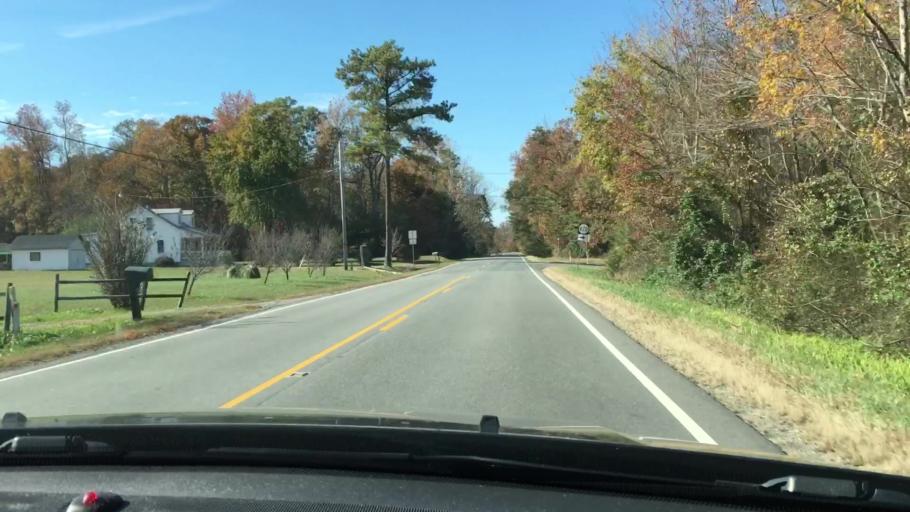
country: US
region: Virginia
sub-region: King William County
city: King William
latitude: 37.6735
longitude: -76.9781
